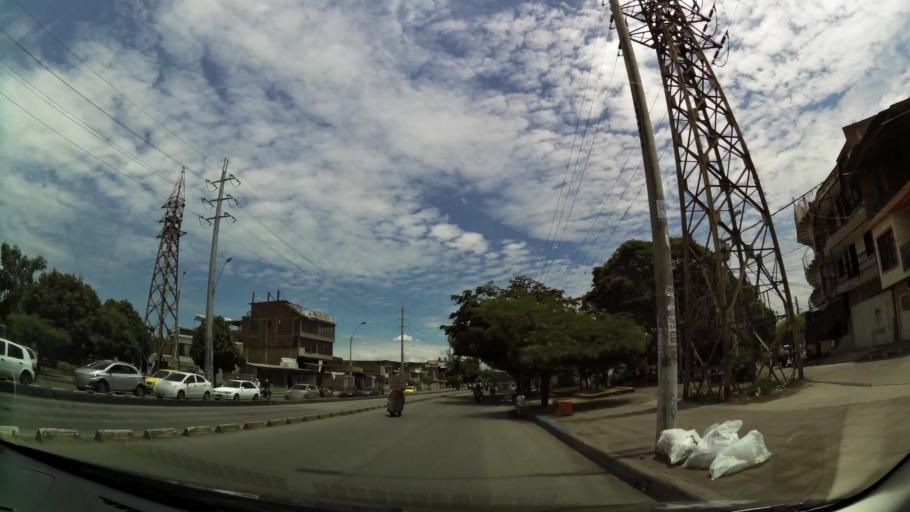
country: CO
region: Valle del Cauca
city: Cali
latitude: 3.4442
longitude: -76.4898
